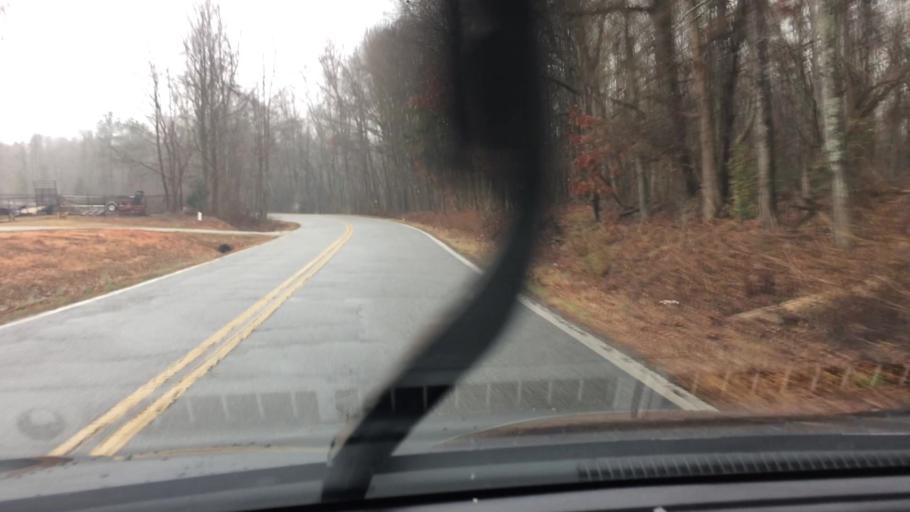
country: US
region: South Carolina
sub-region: Anderson County
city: Williamston
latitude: 34.6355
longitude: -82.4803
